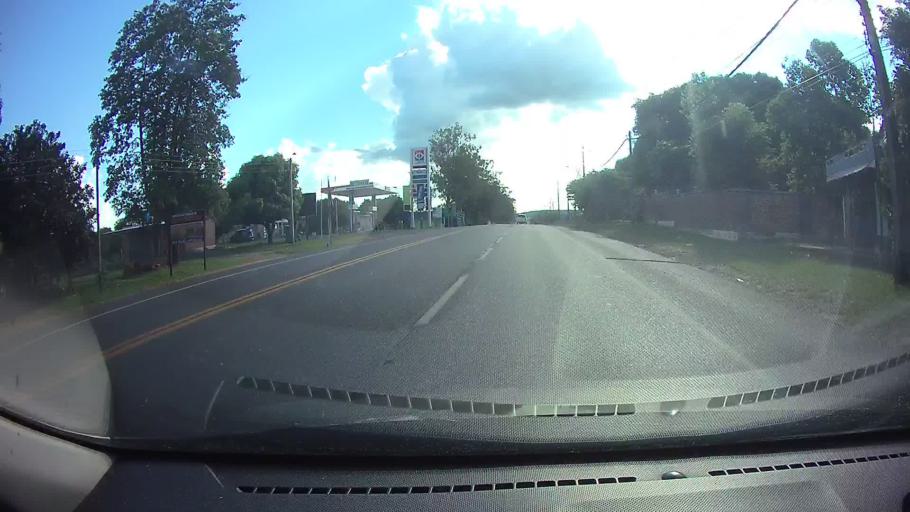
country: PY
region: Cordillera
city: Eusebio Ayala
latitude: -25.3828
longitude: -57.0471
